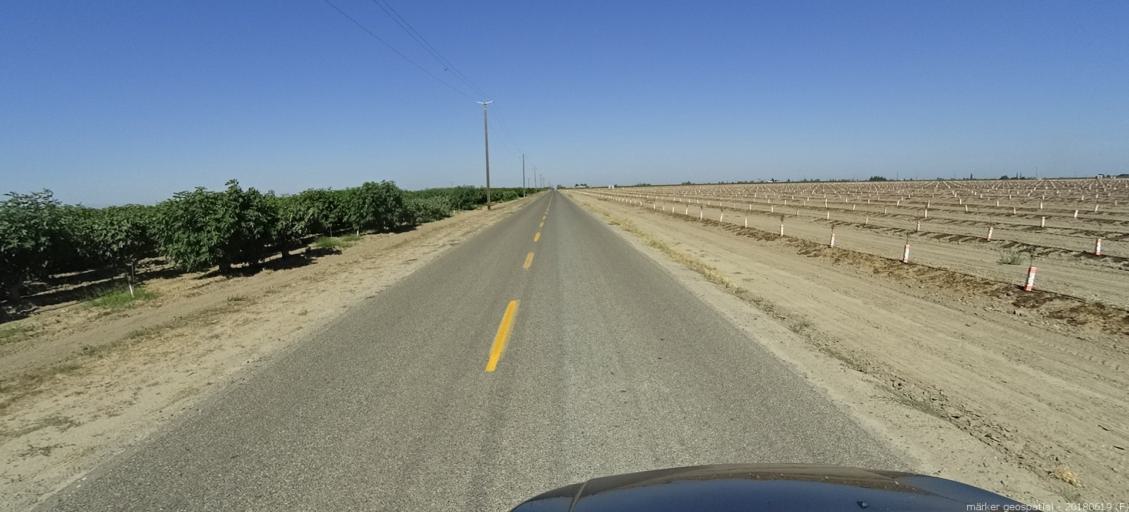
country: US
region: California
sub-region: Fresno County
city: Biola
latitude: 36.8368
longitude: -120.0204
